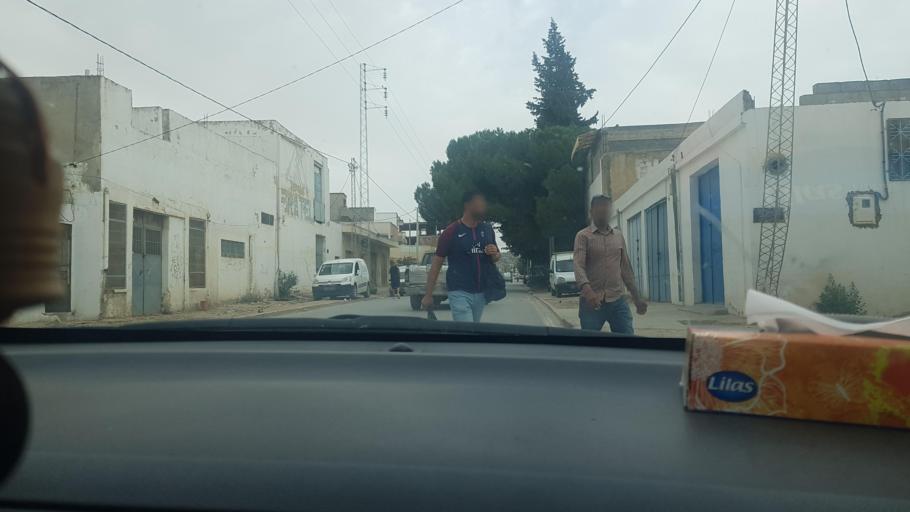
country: TN
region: Tunis
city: Oued Lill
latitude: 36.8321
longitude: 10.0446
